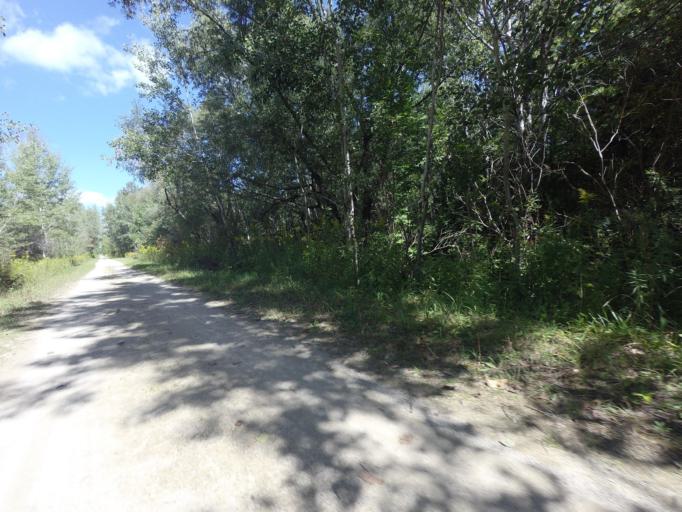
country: CA
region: Ontario
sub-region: Wellington County
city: Guelph
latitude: 43.7567
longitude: -80.3223
